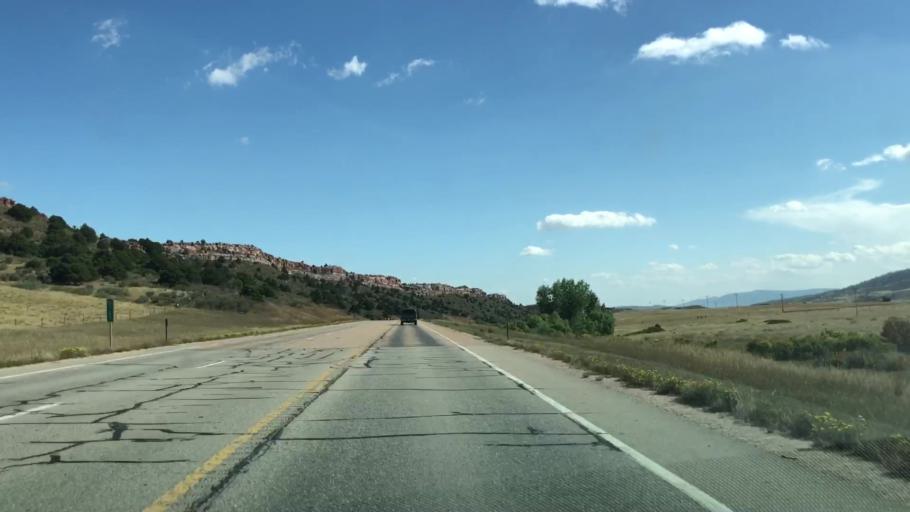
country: US
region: Colorado
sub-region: Larimer County
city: Laporte
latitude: 40.7828
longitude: -105.1879
